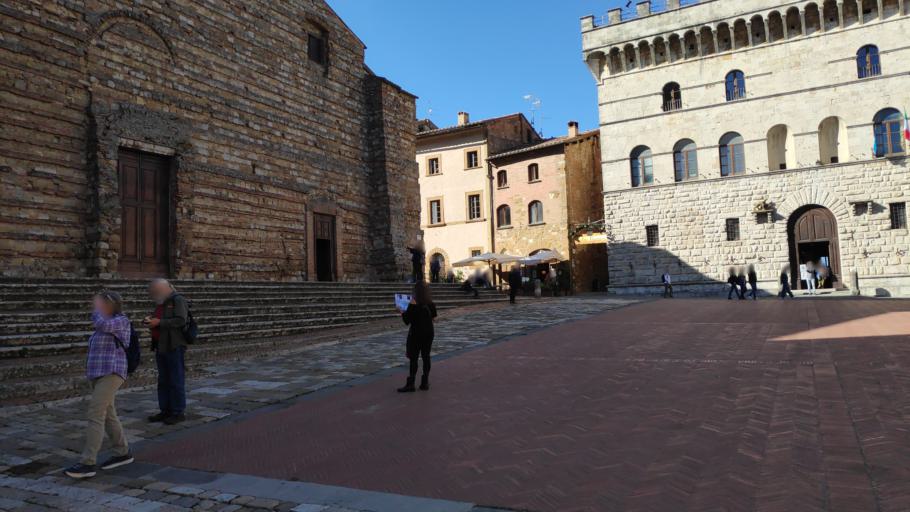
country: IT
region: Tuscany
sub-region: Provincia di Siena
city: Montepulciano
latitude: 43.0926
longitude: 11.7812
